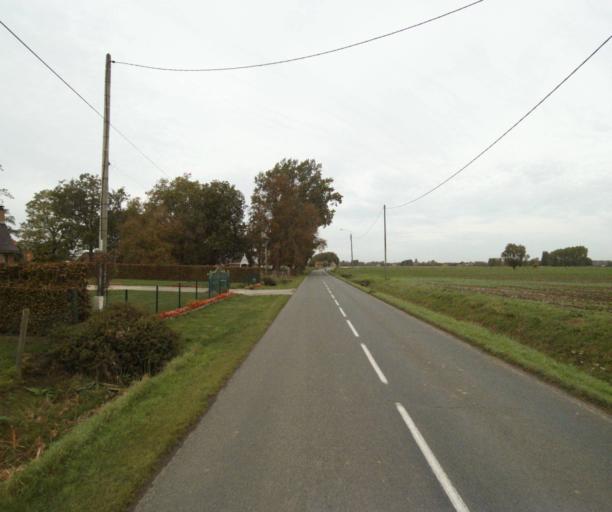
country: FR
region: Nord-Pas-de-Calais
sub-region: Departement du Nord
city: Aubers
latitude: 50.5989
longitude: 2.8080
